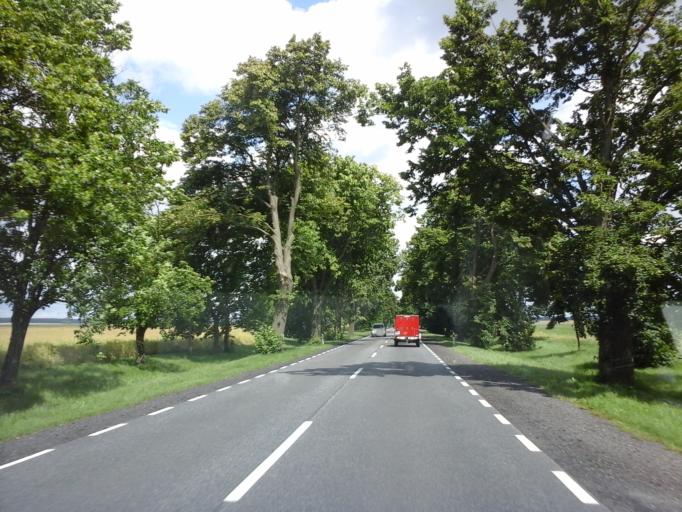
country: PL
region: Lubusz
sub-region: Powiat strzelecko-drezdenecki
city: Strzelce Krajenskie
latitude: 52.8930
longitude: 15.5719
